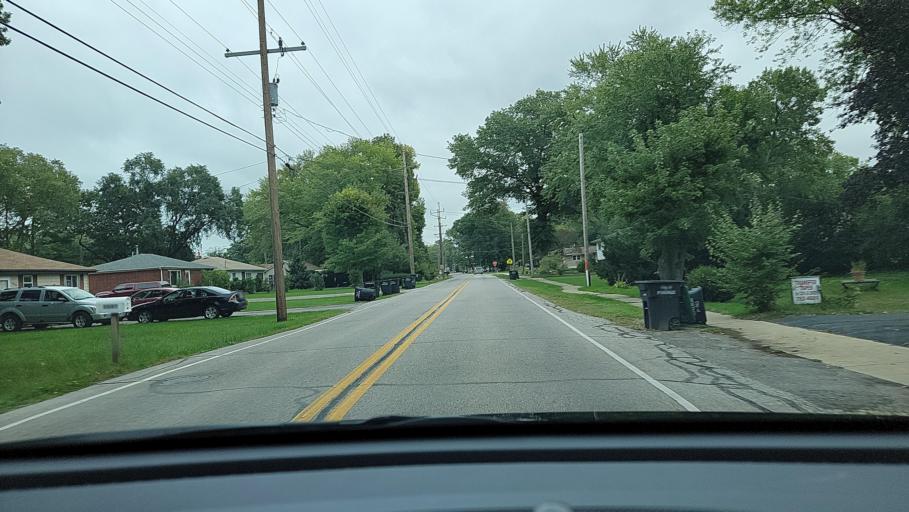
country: US
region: Indiana
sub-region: Porter County
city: Portage
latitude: 41.5717
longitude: -87.1879
